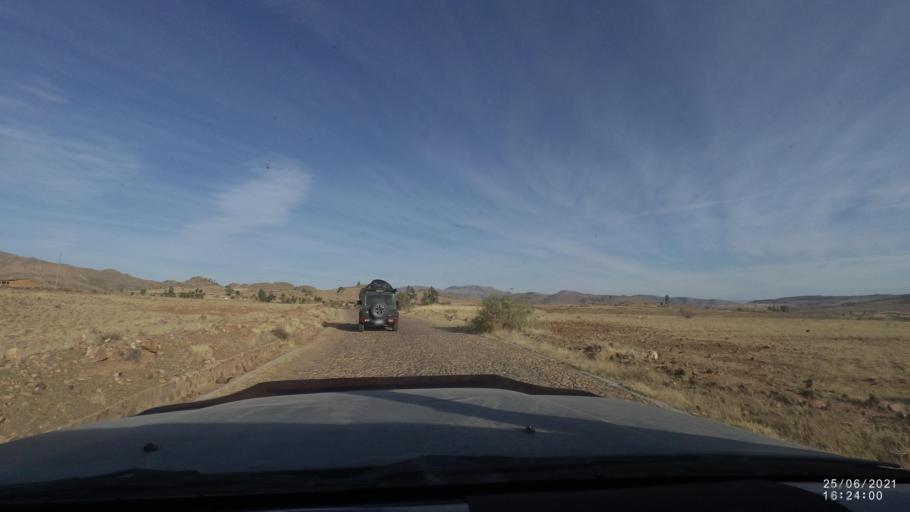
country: BO
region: Cochabamba
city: Arani
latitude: -17.7629
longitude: -65.8279
